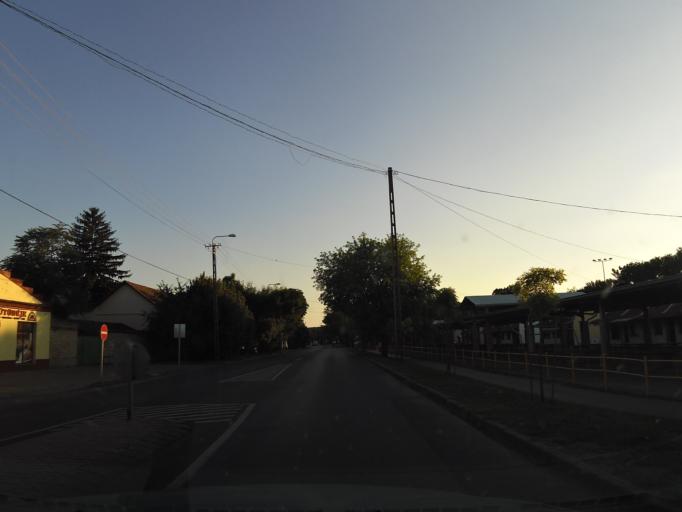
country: HU
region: Csongrad
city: Hodmezovasarhely
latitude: 46.4235
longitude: 20.3356
